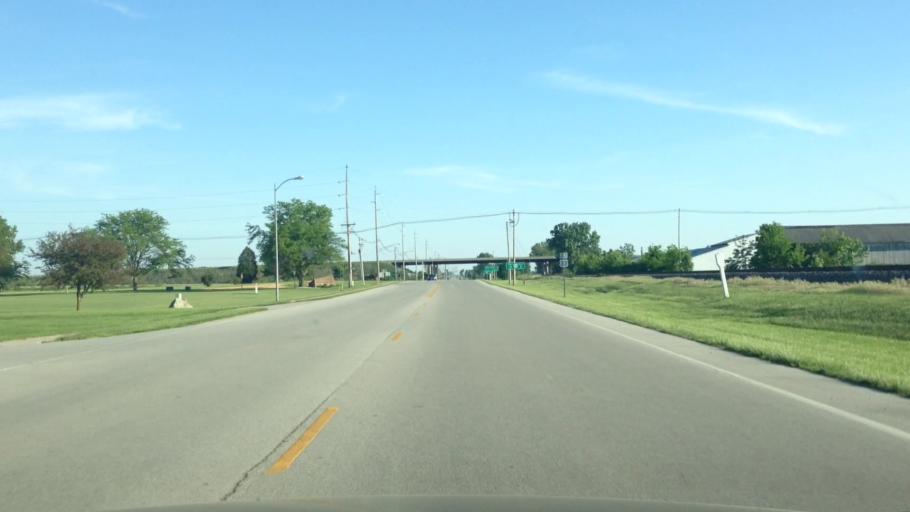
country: US
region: Ohio
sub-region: Auglaize County
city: Wapakoneta
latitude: 40.5598
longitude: -84.1941
